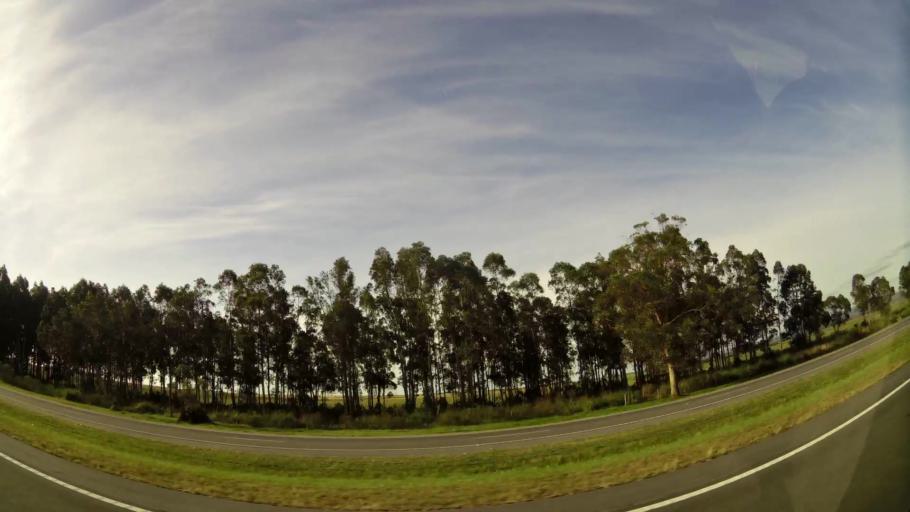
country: UY
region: Lavalleja
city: Solis de Mataojo
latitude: -34.7800
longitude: -55.4721
